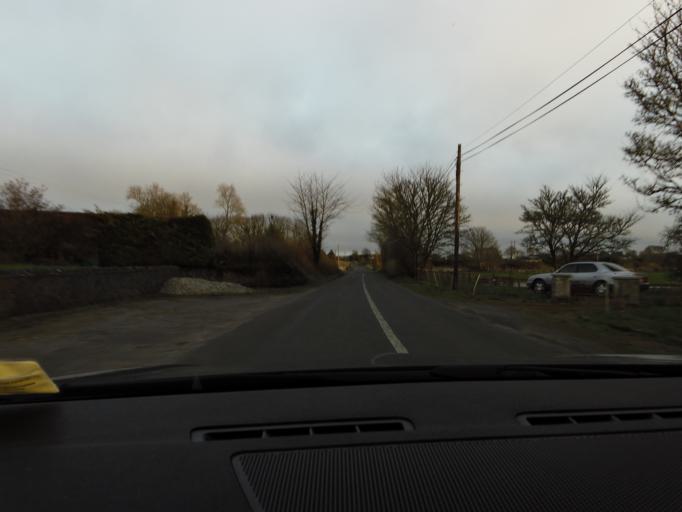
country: IE
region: Connaught
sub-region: Sligo
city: Ballymote
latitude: 54.0241
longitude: -8.5672
